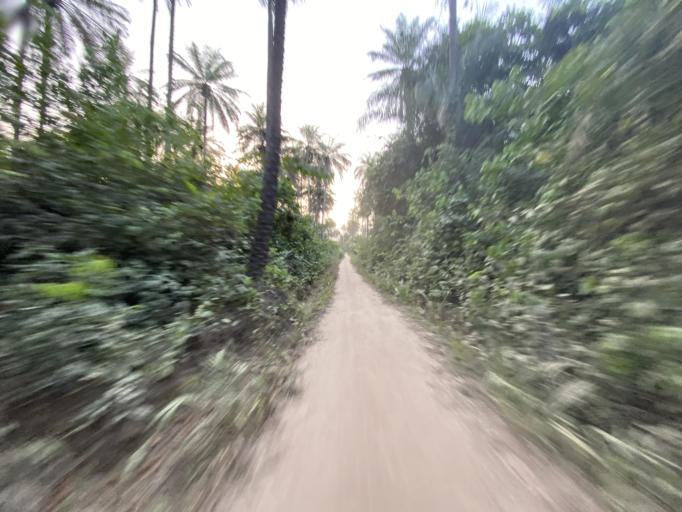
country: GW
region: Tombali
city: Quebo
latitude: 10.8947
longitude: -15.0122
